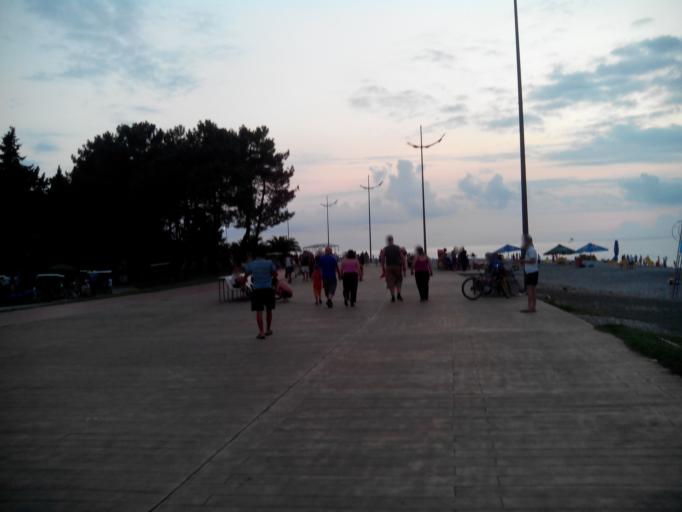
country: GE
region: Ajaria
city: Batumi
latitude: 41.6571
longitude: 41.6388
